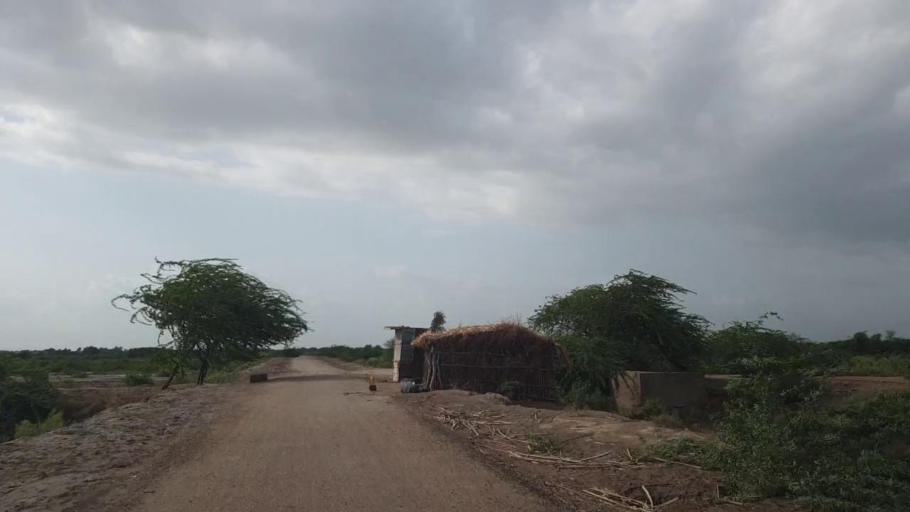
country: PK
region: Sindh
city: Kadhan
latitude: 24.5786
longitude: 69.0590
